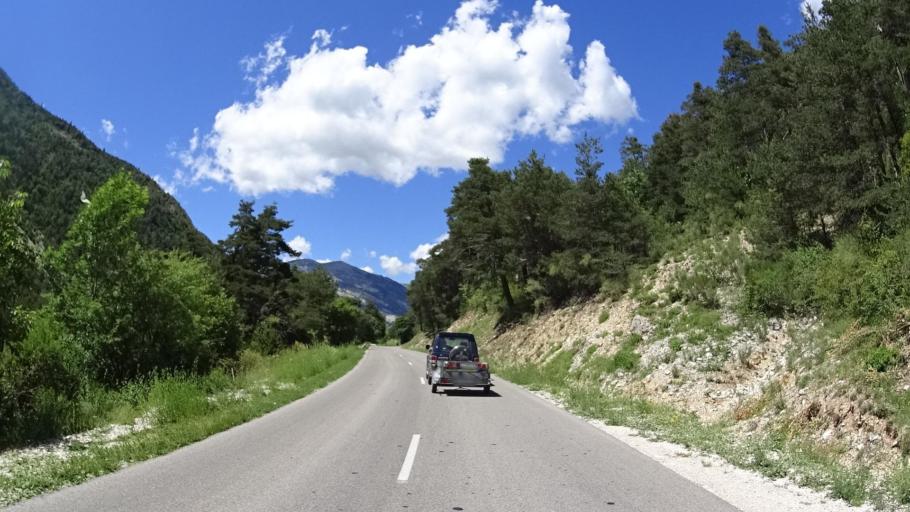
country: FR
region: Provence-Alpes-Cote d'Azur
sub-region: Departement des Alpes-de-Haute-Provence
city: Annot
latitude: 44.0667
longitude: 6.5748
